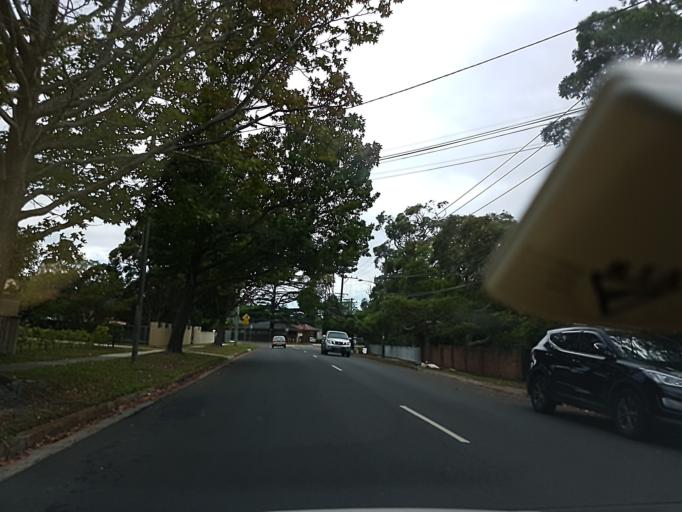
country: AU
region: New South Wales
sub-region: Warringah
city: Davidson
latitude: -33.7391
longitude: 151.2159
